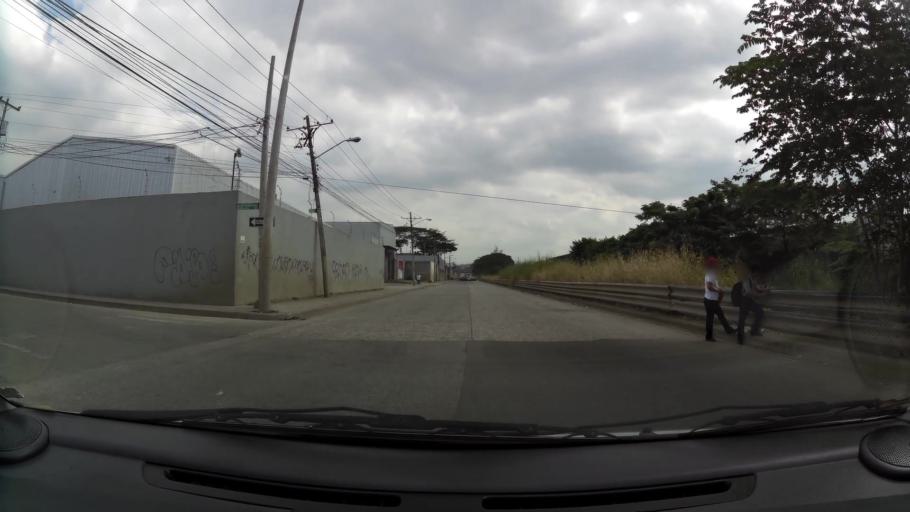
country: EC
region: Guayas
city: Santa Lucia
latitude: -2.1015
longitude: -79.9427
